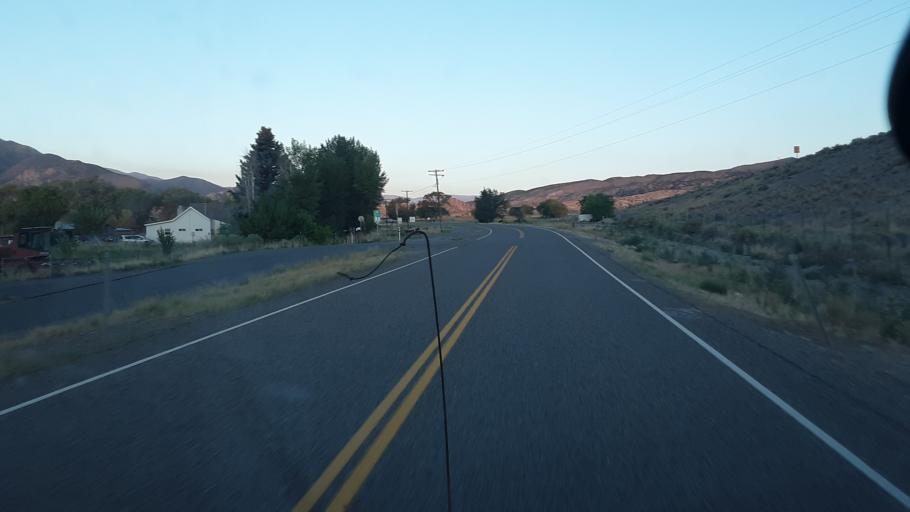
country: US
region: Utah
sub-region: Sevier County
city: Monroe
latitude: 38.6030
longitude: -112.2381
